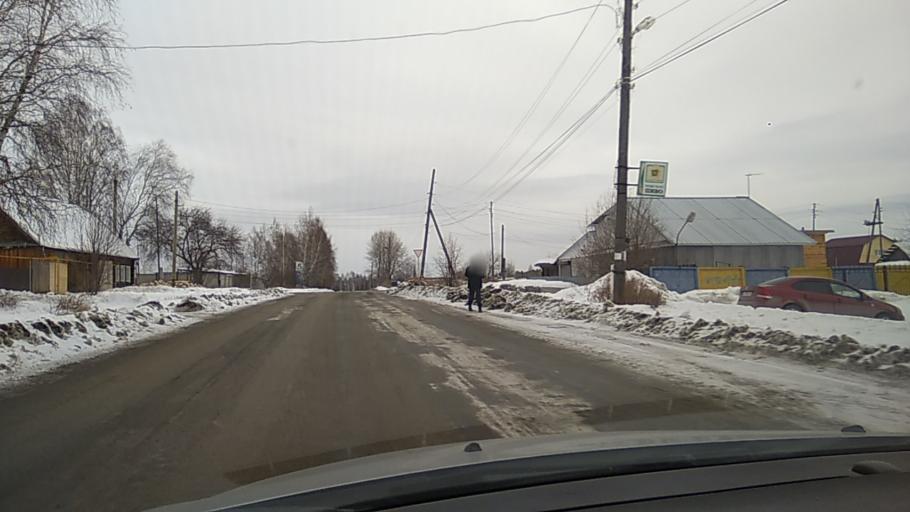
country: RU
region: Sverdlovsk
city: Revda
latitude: 56.8099
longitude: 59.9359
